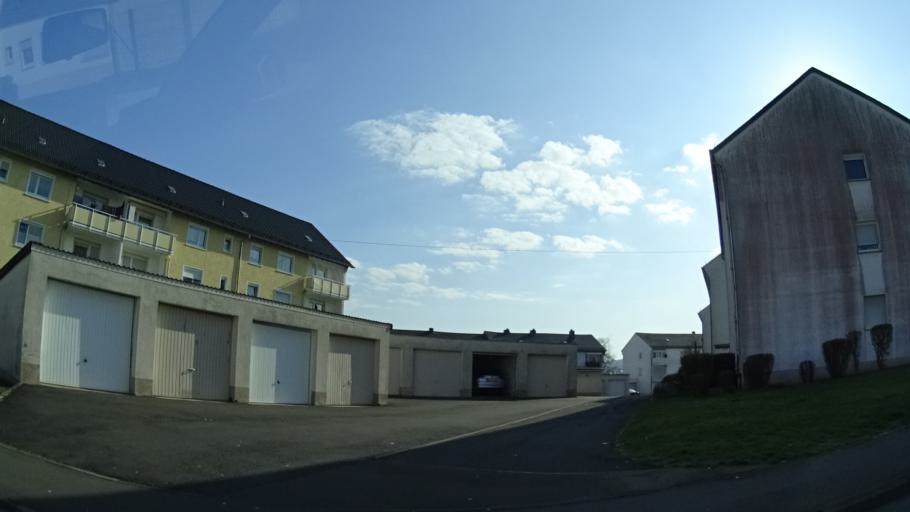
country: DE
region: Rheinland-Pfalz
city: Idar-Oberstein
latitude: 49.6963
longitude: 7.3276
